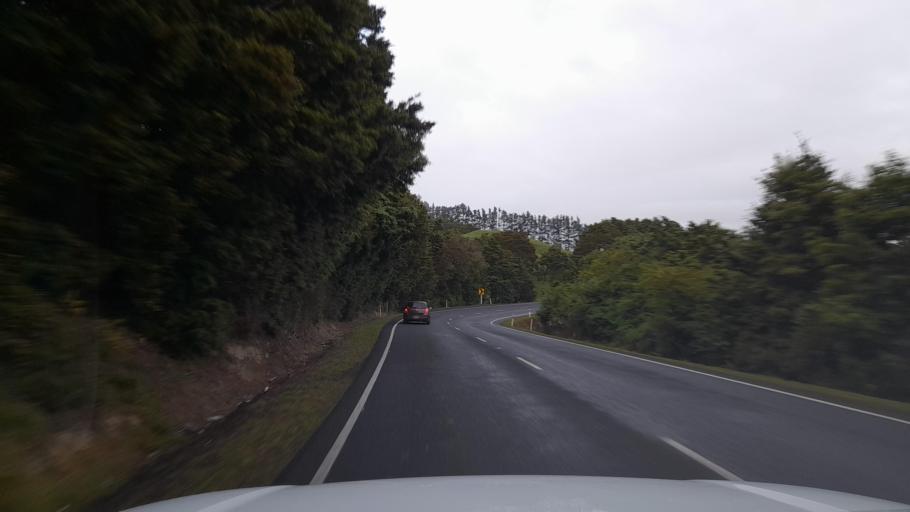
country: NZ
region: Northland
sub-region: Whangarei
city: Maungatapere
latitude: -35.7073
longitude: 174.0089
